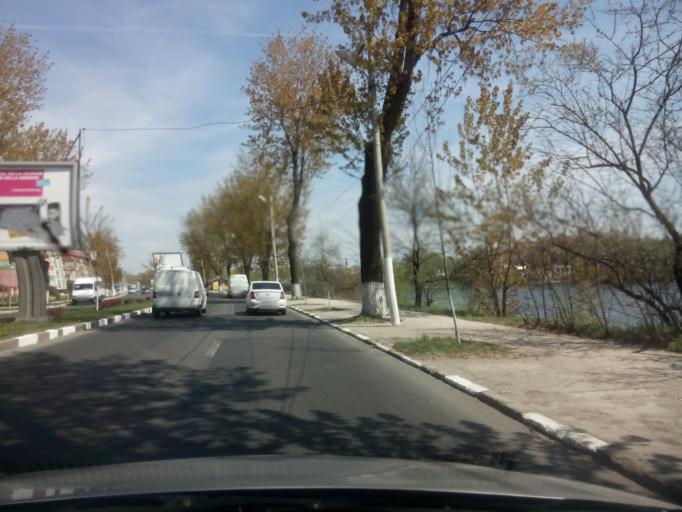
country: RO
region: Ilfov
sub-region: Comuna Pantelimon
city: Pantelimon
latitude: 44.4434
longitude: 26.1993
